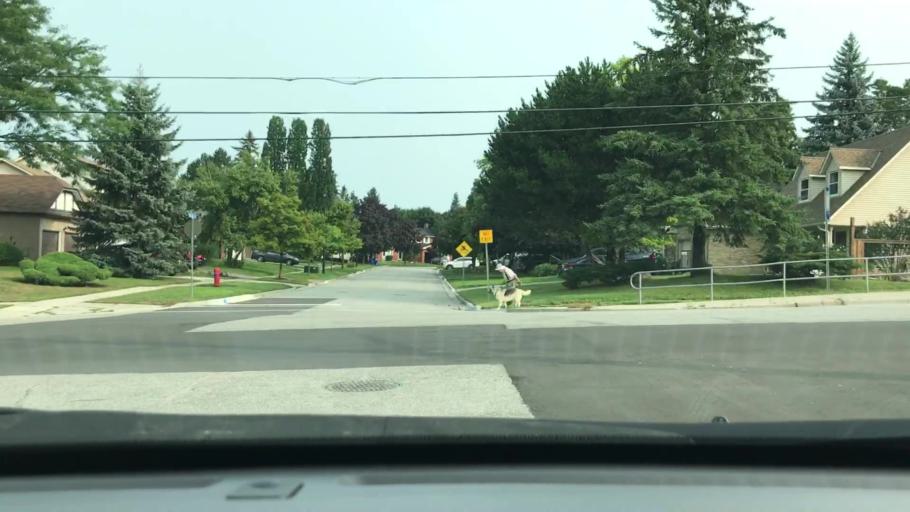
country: CA
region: Ontario
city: Newmarket
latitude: 44.0561
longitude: -79.4323
